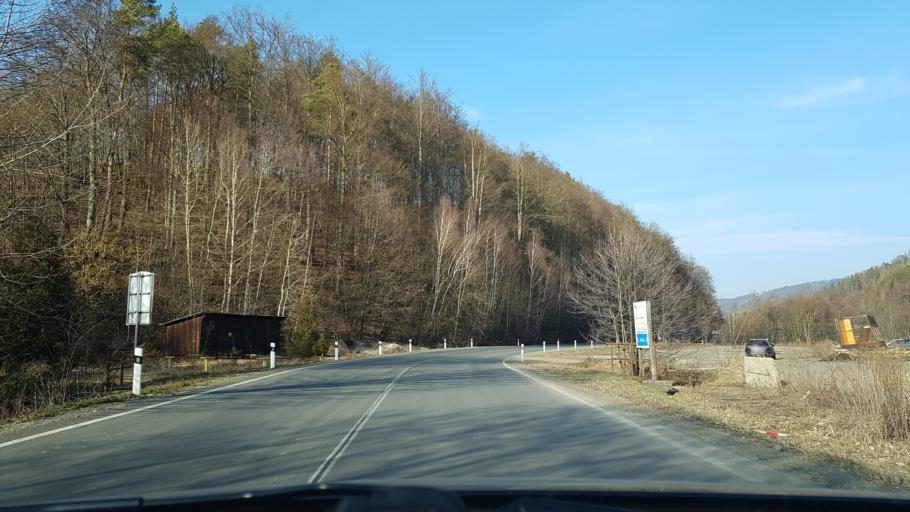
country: CZ
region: Olomoucky
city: Ruda nad Moravou
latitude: 49.9859
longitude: 16.8889
